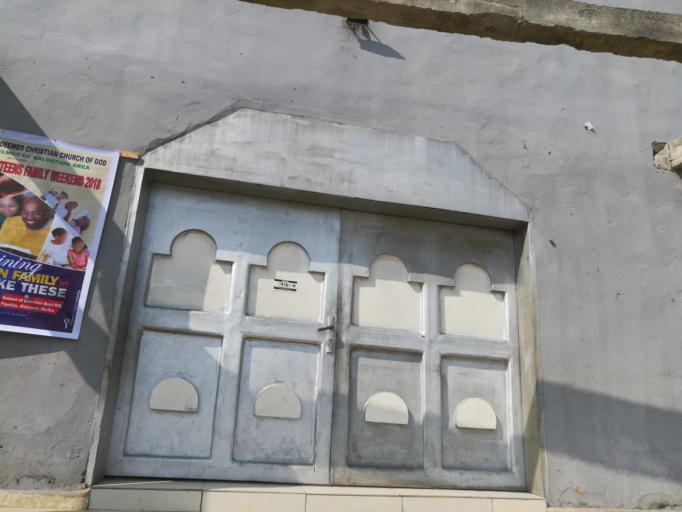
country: NG
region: Rivers
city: Okrika
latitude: 4.7573
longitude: 7.0984
